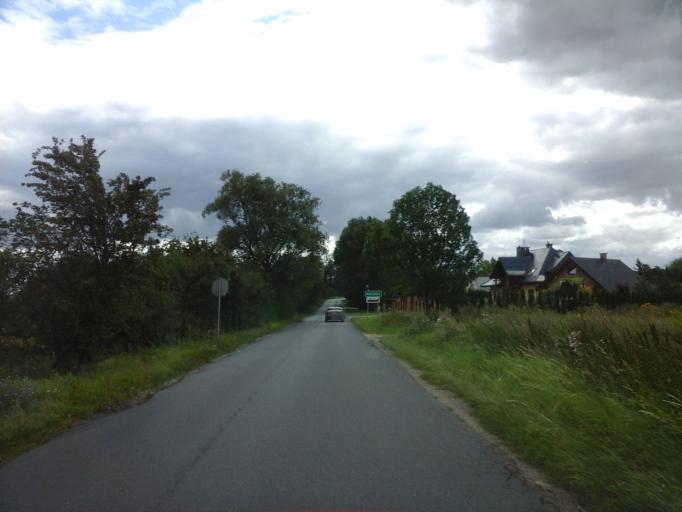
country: PL
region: West Pomeranian Voivodeship
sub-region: Powiat policki
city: Przeclaw
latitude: 53.3984
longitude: 14.4378
